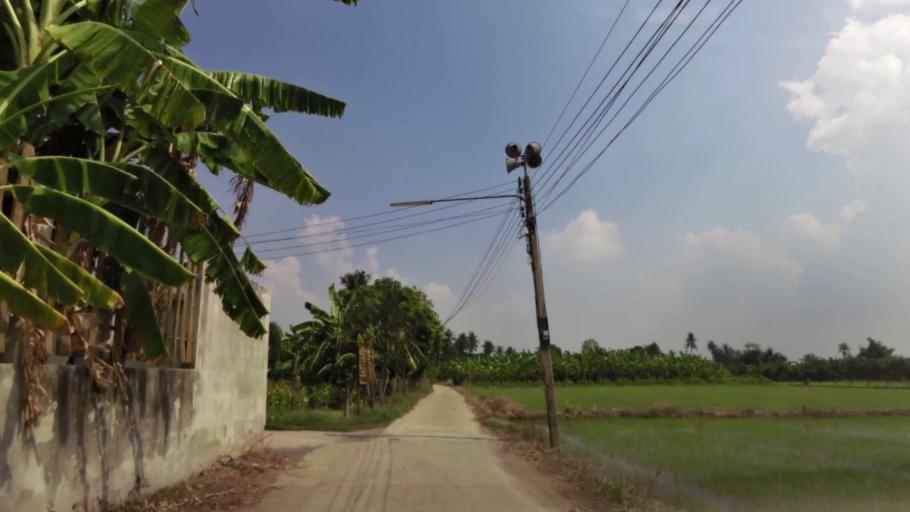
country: TH
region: Ang Thong
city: Ang Thong
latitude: 14.6069
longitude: 100.4030
